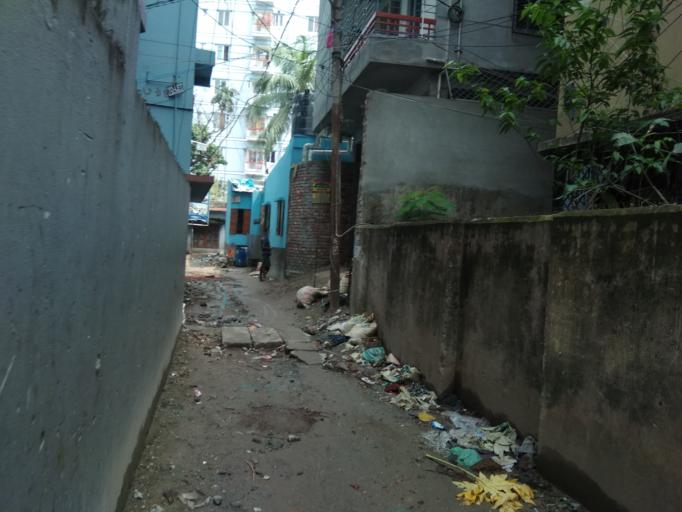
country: BD
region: Dhaka
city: Azimpur
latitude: 23.8004
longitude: 90.3741
